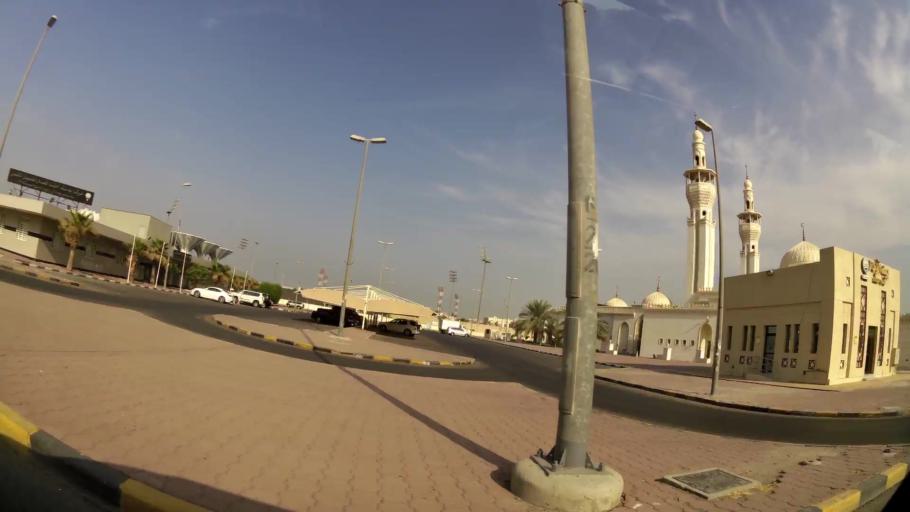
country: KW
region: Al Asimah
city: Ash Shamiyah
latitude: 29.3269
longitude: 47.9820
